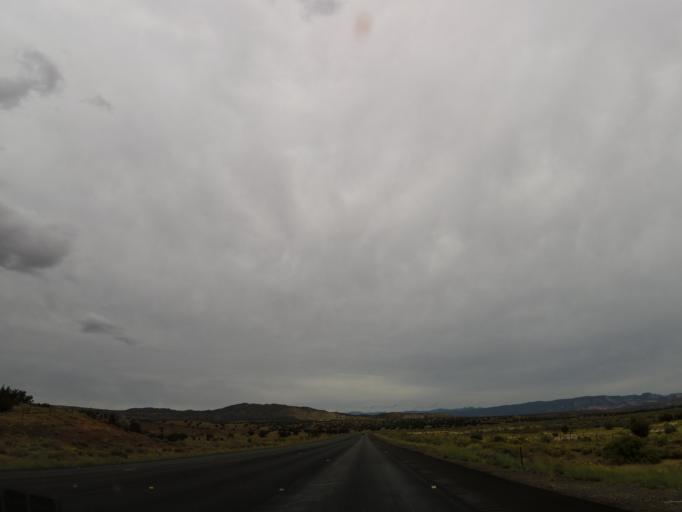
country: US
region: New Mexico
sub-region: Sandoval County
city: Jemez Pueblo
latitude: 35.5483
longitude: -106.8249
